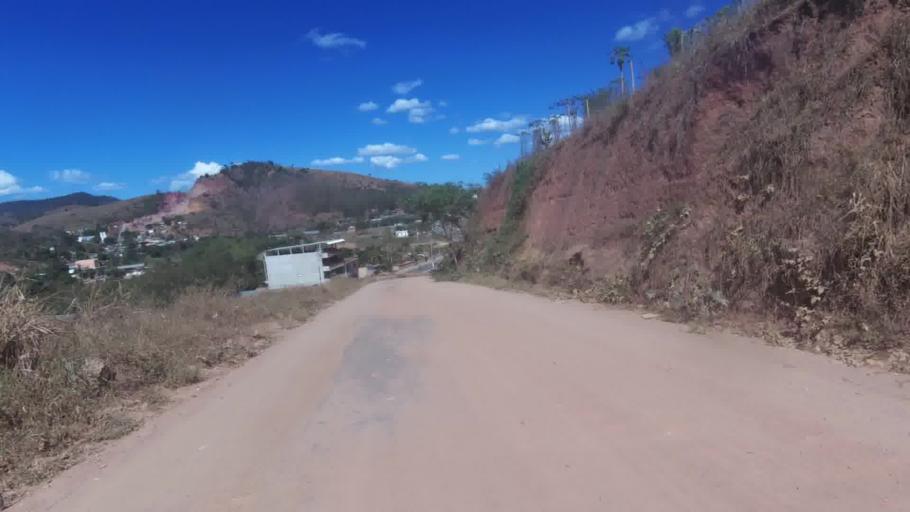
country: BR
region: Espirito Santo
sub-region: Cachoeiro De Itapemirim
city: Cachoeiro de Itapemirim
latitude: -20.9185
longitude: -41.1918
